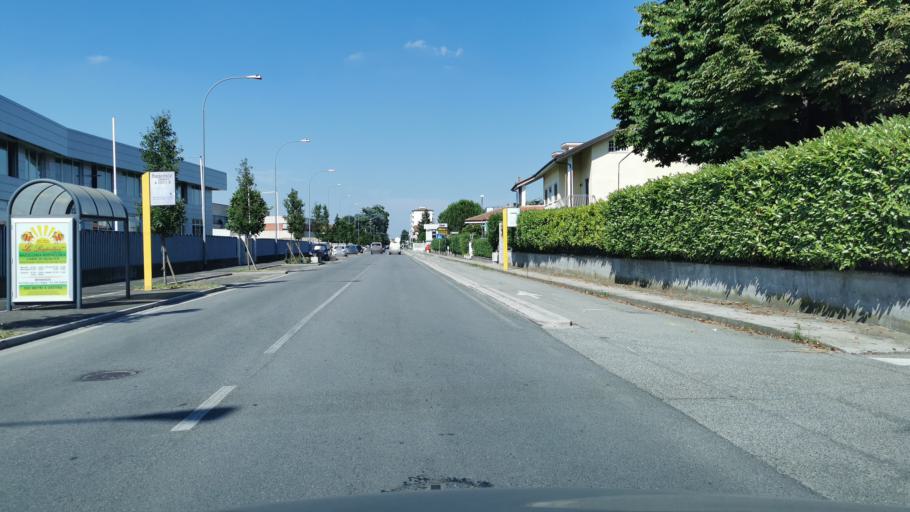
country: IT
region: Piedmont
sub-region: Provincia di Torino
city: Brandizzo
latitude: 45.1708
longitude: 7.8267
